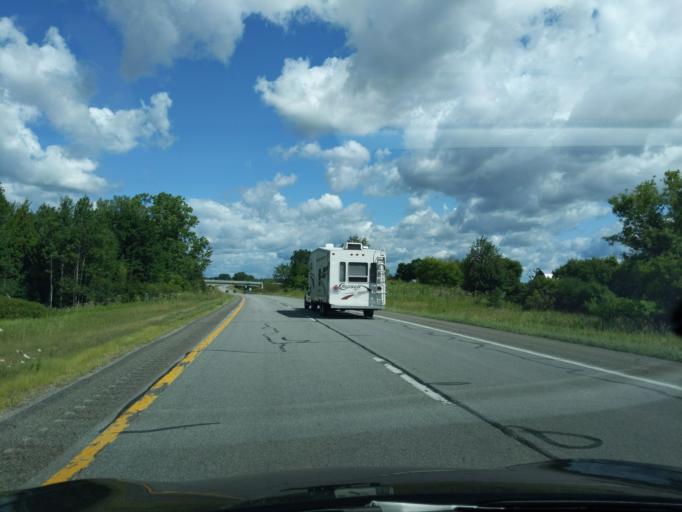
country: US
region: Michigan
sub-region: Clare County
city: Clare
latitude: 43.7539
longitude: -84.7572
